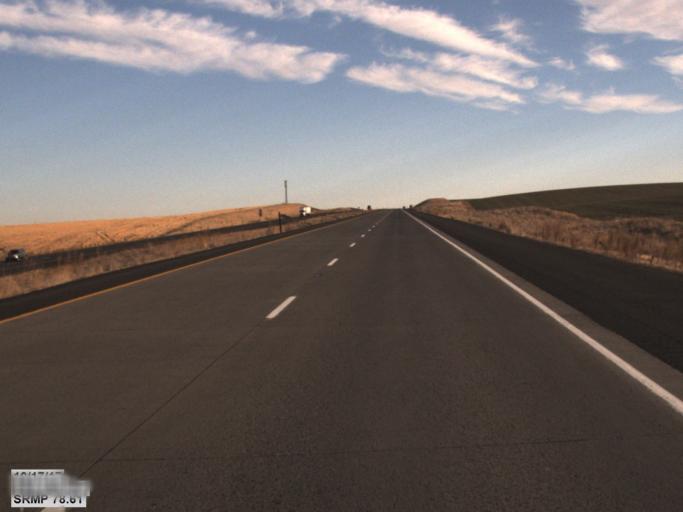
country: US
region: Washington
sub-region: Adams County
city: Ritzville
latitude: 46.9229
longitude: -118.5976
